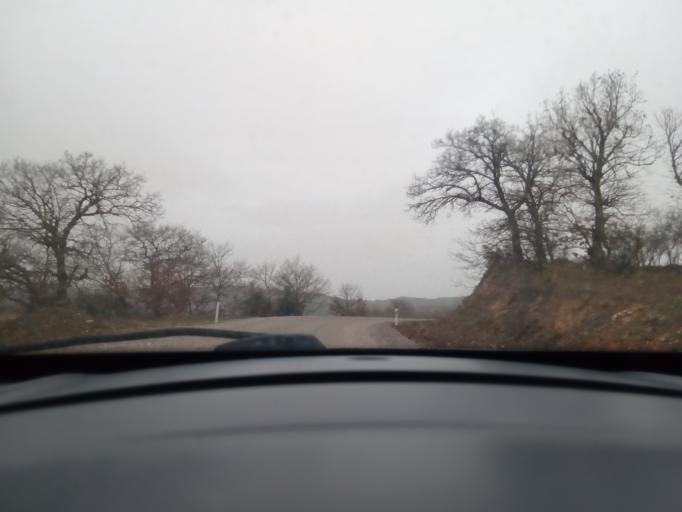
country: TR
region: Balikesir
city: Susurluk
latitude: 39.9188
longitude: 28.0813
